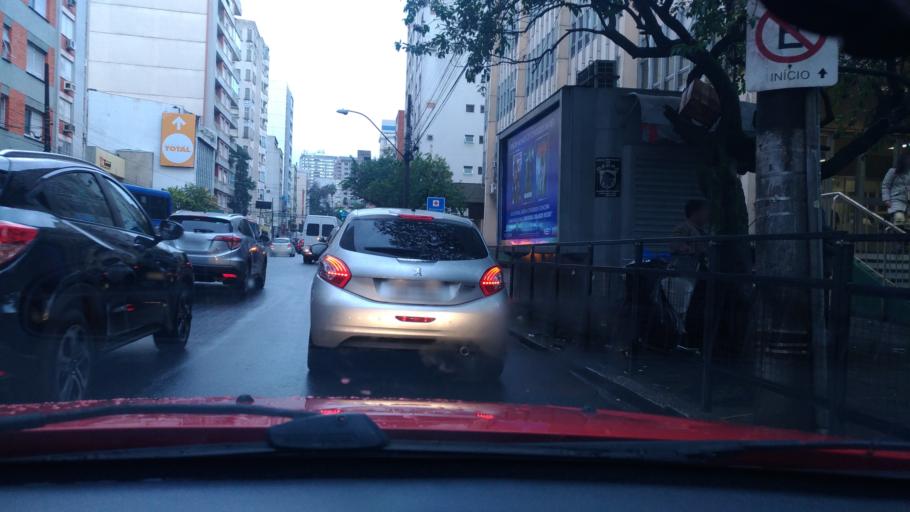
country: BR
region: Rio Grande do Sul
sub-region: Porto Alegre
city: Porto Alegre
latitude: -30.0294
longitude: -51.2150
